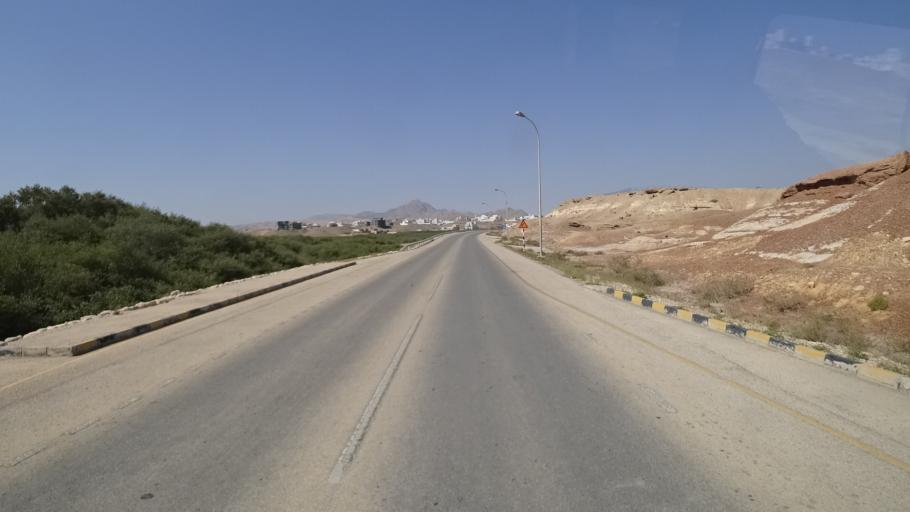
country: OM
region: Ash Sharqiyah
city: Sur
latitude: 22.5651
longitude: 59.5099
